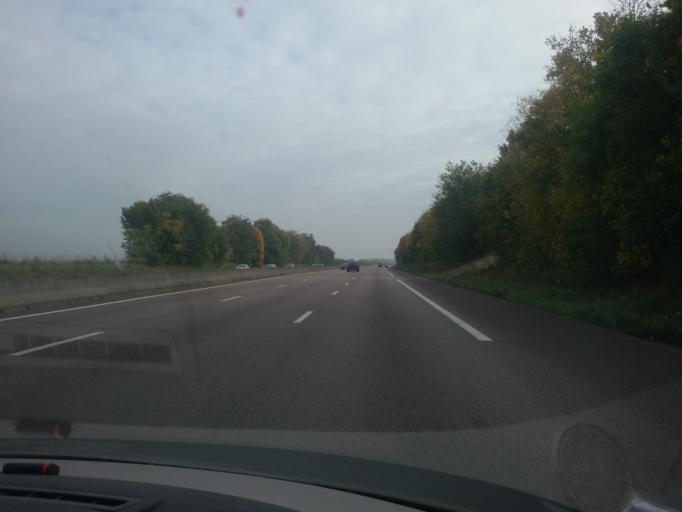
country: FR
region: Haute-Normandie
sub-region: Departement de l'Eure
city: La Chapelle-Reanville
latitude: 49.0731
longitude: 1.4025
